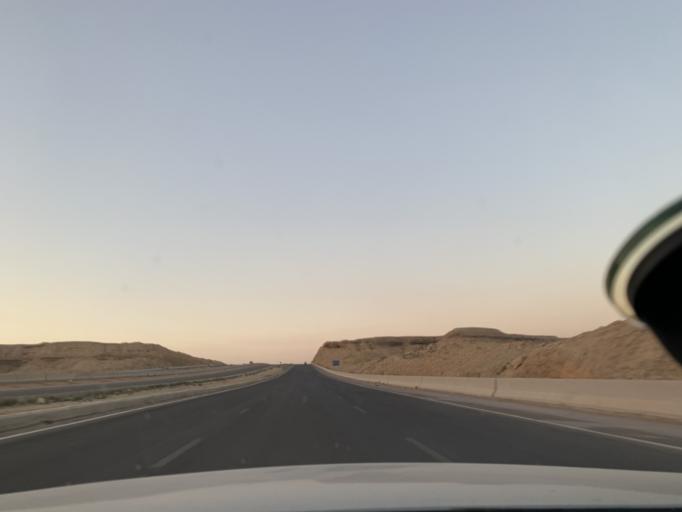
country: EG
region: Muhafazat al Qahirah
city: Halwan
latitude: 29.9465
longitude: 31.5355
